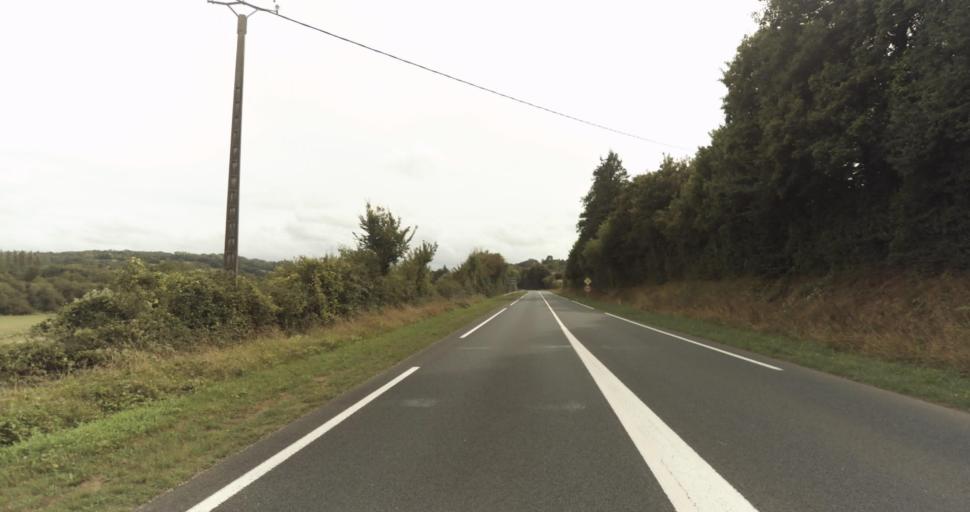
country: FR
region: Lower Normandy
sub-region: Departement de l'Orne
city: Gace
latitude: 48.8297
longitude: 0.2741
